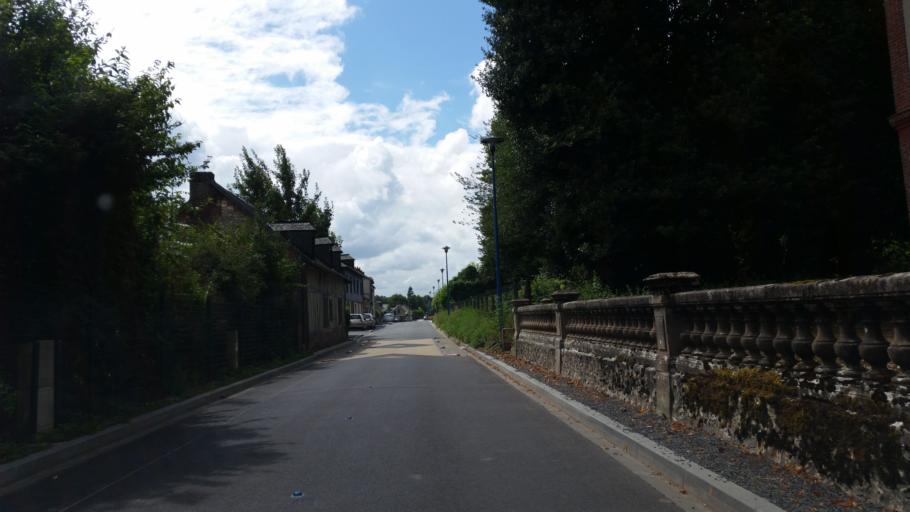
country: FR
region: Lower Normandy
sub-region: Departement du Calvados
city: La Riviere-Saint-Sauveur
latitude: 49.3867
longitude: 0.2448
